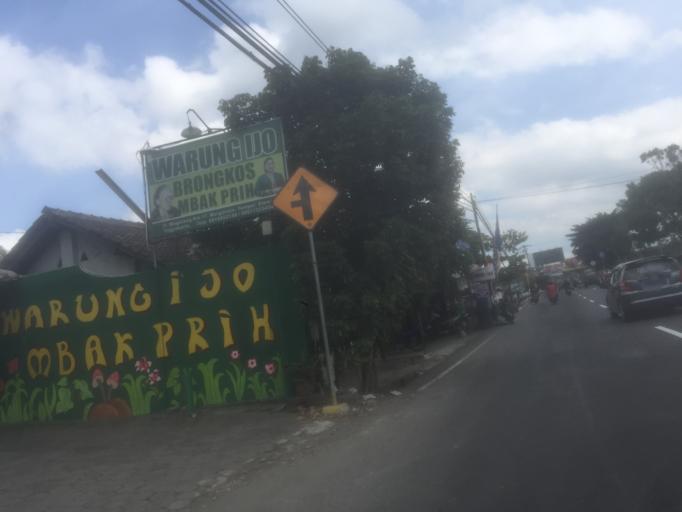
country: ID
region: Daerah Istimewa Yogyakarta
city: Sleman
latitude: -7.6594
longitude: 110.3274
